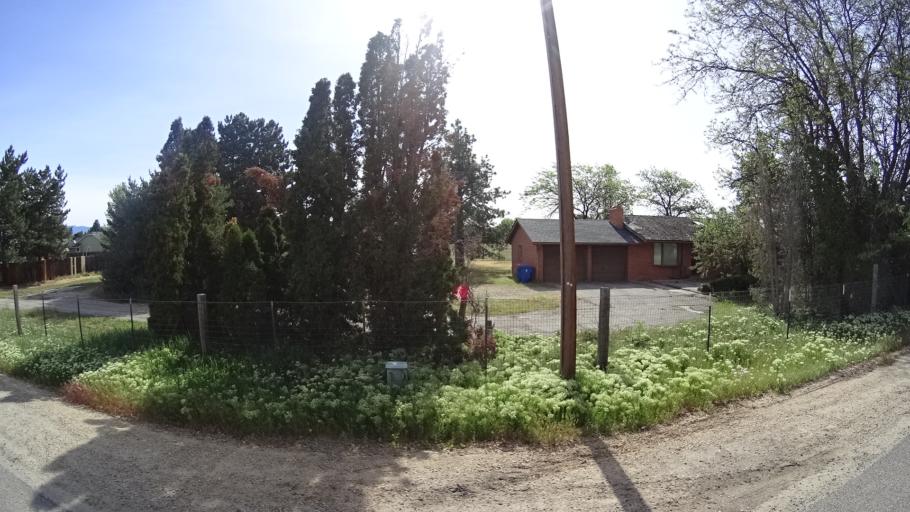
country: US
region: Idaho
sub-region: Ada County
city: Meridian
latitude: 43.5644
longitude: -116.3343
